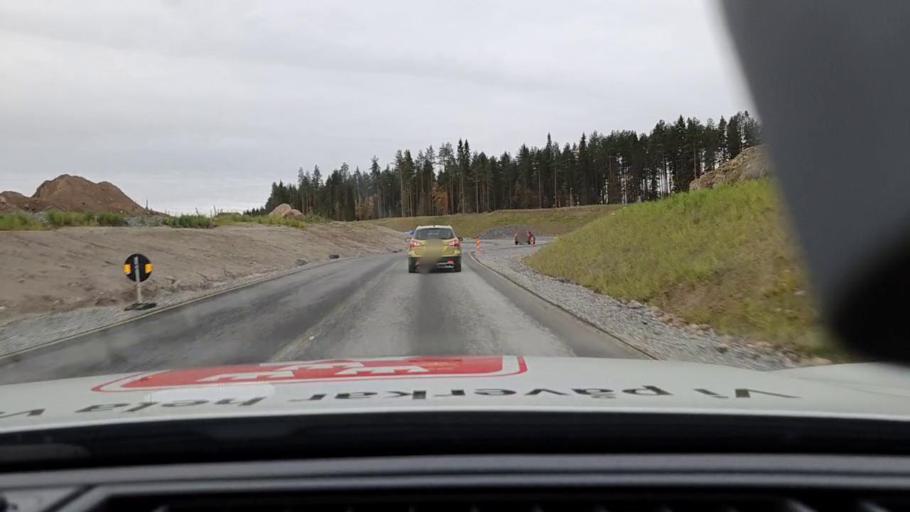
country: SE
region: Norrbotten
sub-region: Bodens Kommun
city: Saevast
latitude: 65.7539
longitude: 21.7639
